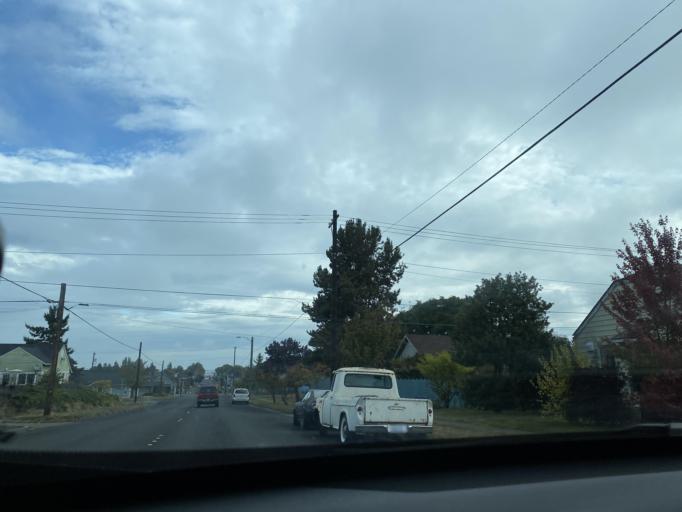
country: US
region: Washington
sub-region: Clallam County
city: Port Angeles
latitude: 48.1091
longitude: -123.4350
